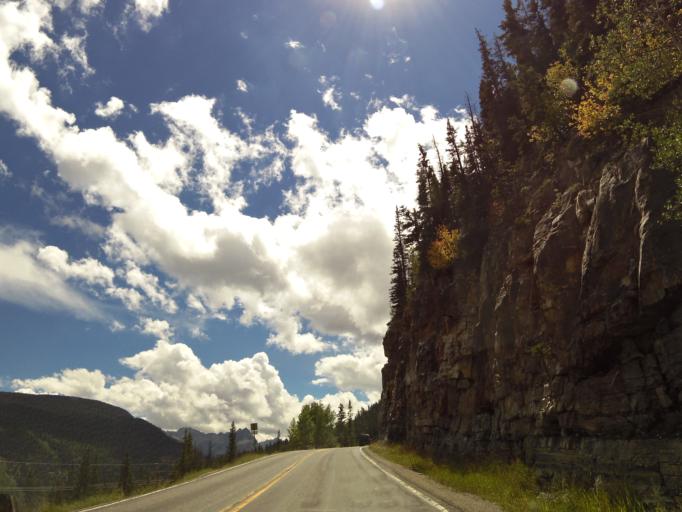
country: US
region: Colorado
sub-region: San Juan County
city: Silverton
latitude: 37.7837
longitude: -107.6717
